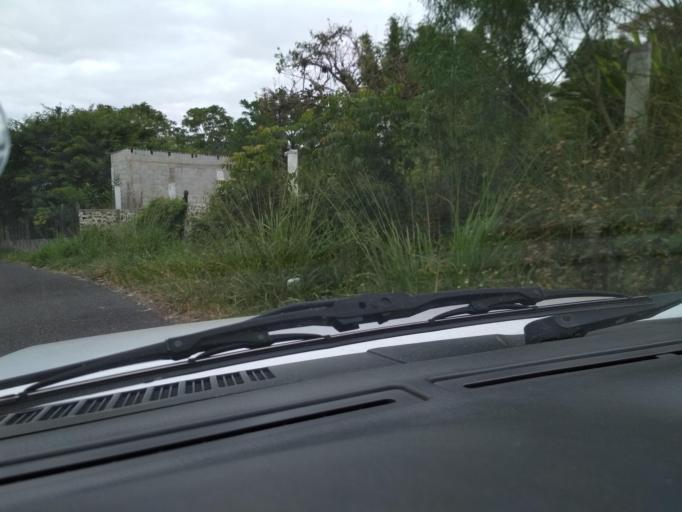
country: MX
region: Veracruz
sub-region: Actopan
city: Trapiche del Rosario
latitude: 19.5836
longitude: -96.7947
